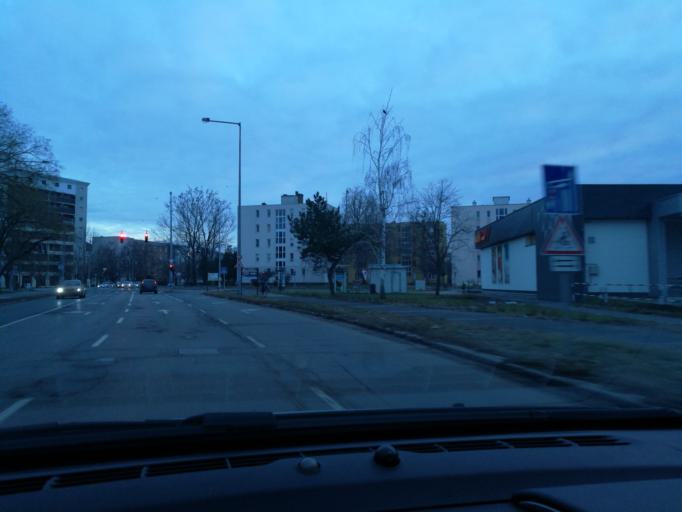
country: HU
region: Szabolcs-Szatmar-Bereg
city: Nyiregyhaza
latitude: 47.9663
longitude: 21.7099
